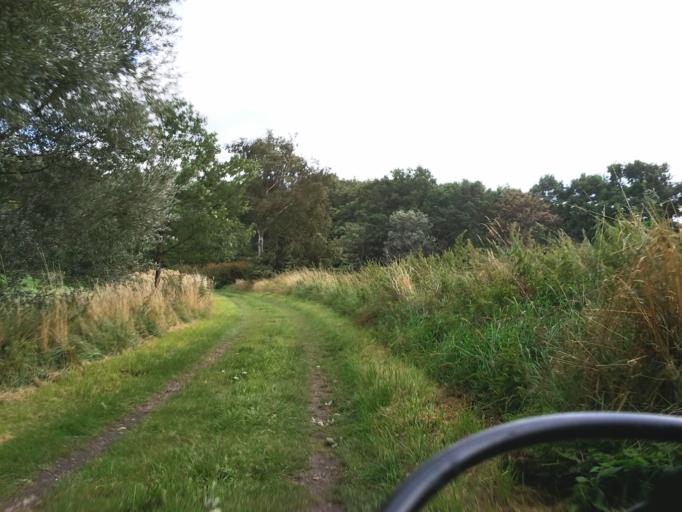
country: DE
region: Mecklenburg-Vorpommern
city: Dierkow-West
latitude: 54.1060
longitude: 12.1325
